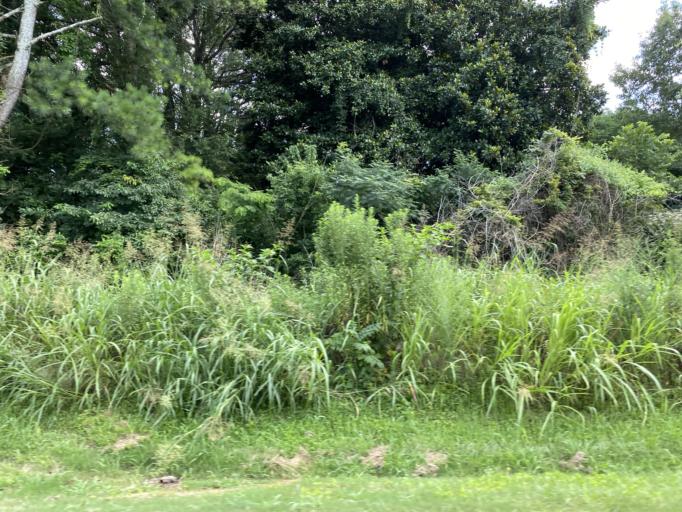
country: US
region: Alabama
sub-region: Madison County
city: Redstone Arsenal
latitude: 34.7570
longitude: -86.6677
